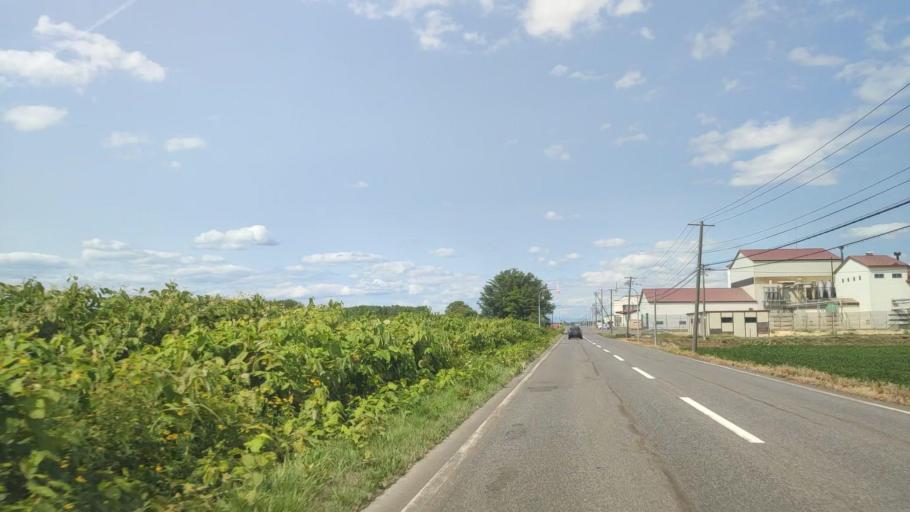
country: JP
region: Hokkaido
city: Nayoro
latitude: 44.2026
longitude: 142.4158
